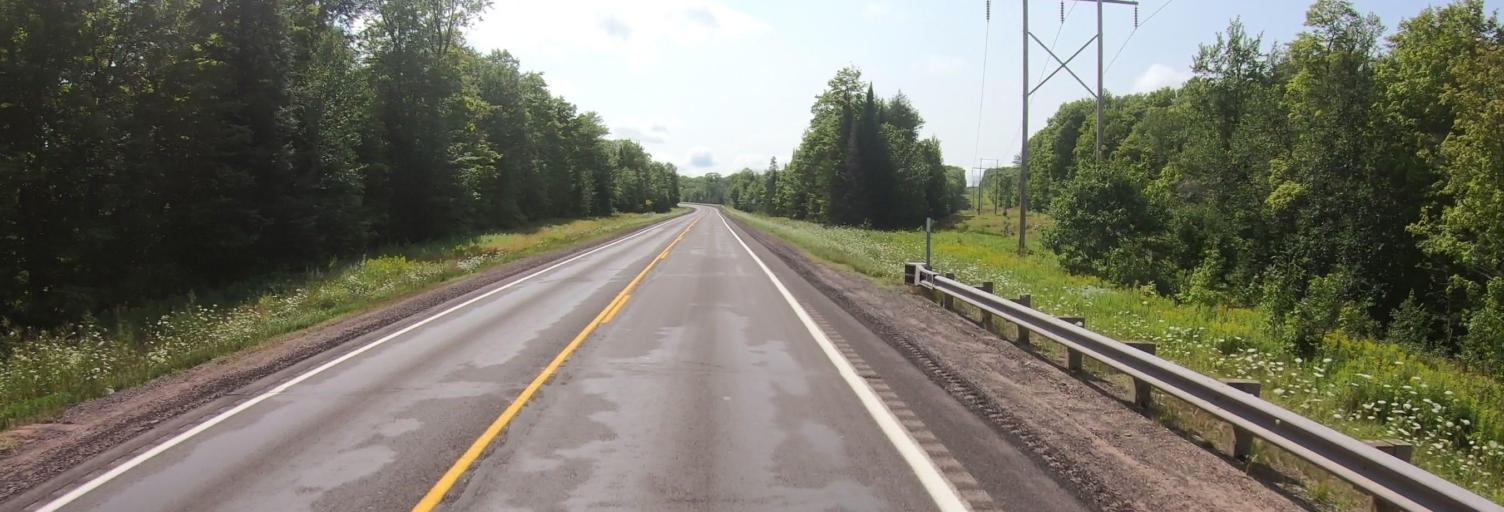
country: US
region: Michigan
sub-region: Ontonagon County
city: Ontonagon
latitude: 46.8513
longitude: -88.9689
